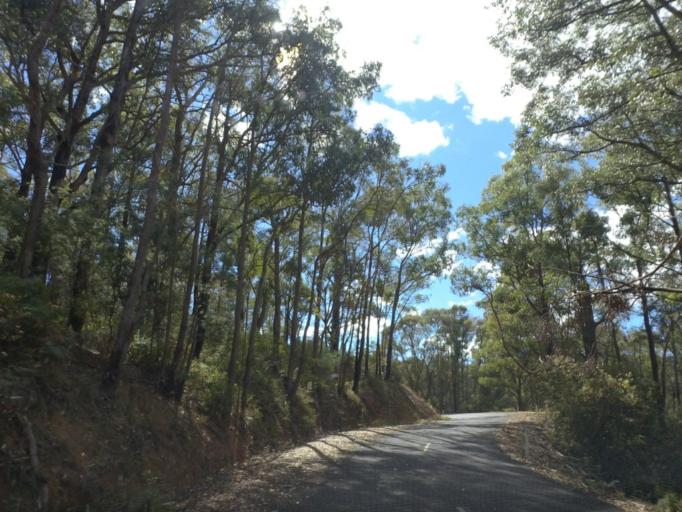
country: AU
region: Victoria
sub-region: Murrindindi
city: Alexandra
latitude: -37.3280
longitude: 145.9434
